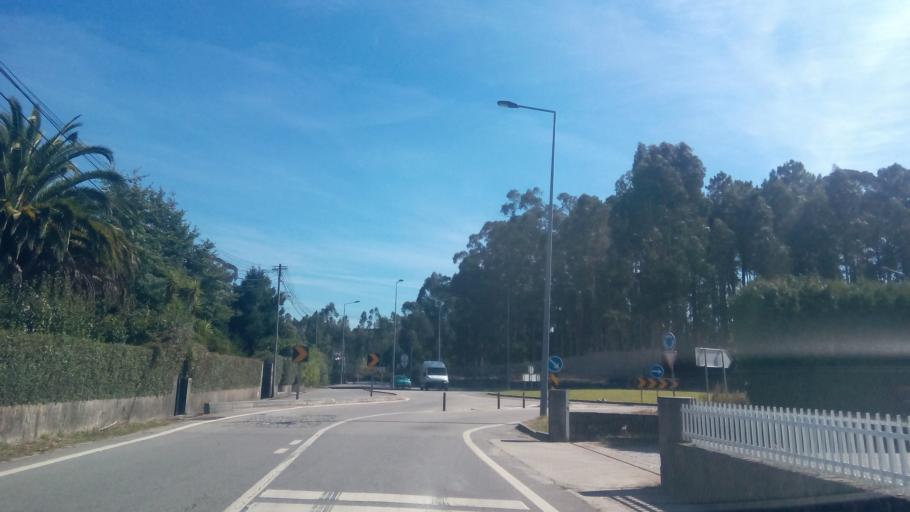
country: PT
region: Porto
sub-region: Paredes
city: Baltar
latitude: 41.1770
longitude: -8.3856
